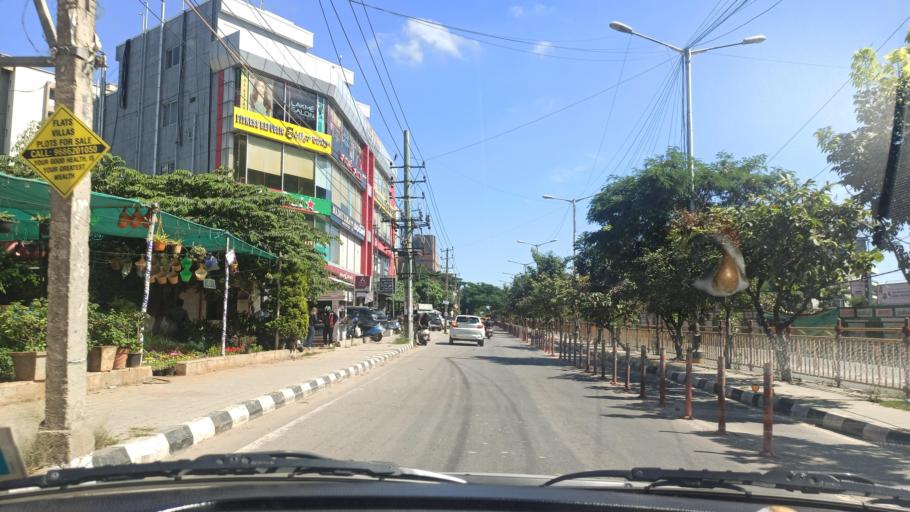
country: IN
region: Karnataka
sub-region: Bangalore Urban
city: Bangalore
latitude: 12.9222
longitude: 77.6678
